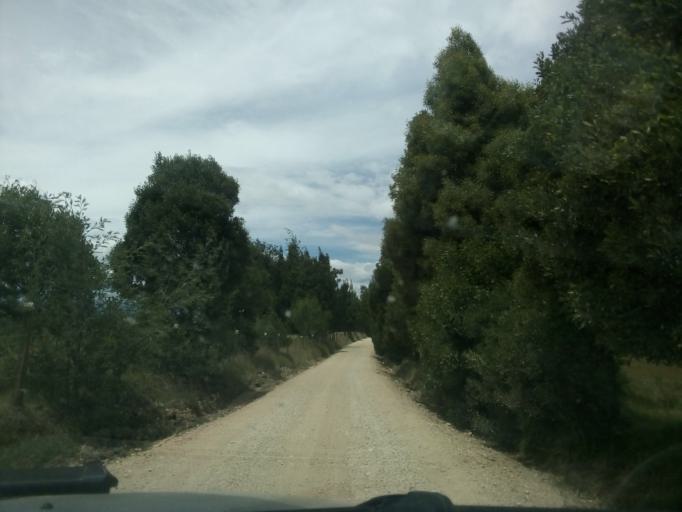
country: CO
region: Boyaca
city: Toca
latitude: 5.5903
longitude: -73.1655
